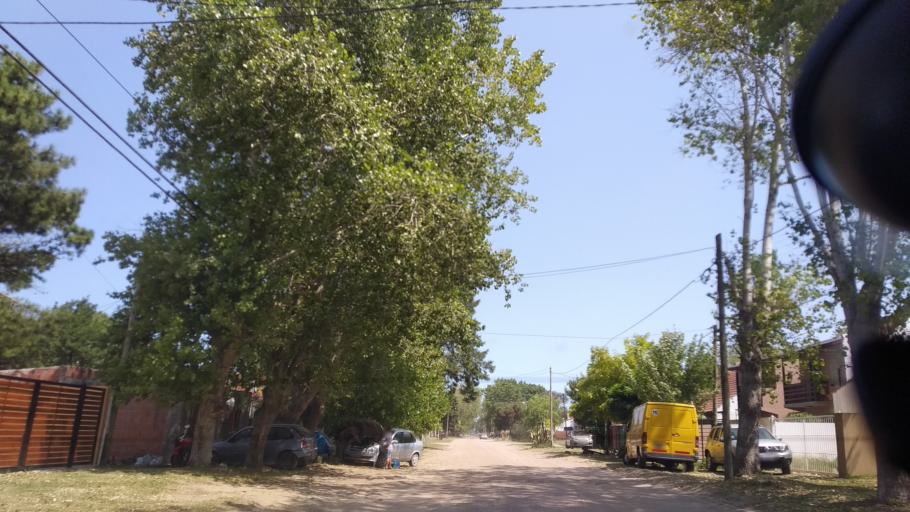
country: AR
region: Buenos Aires
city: Mar del Tuyu
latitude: -36.5670
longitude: -56.6942
